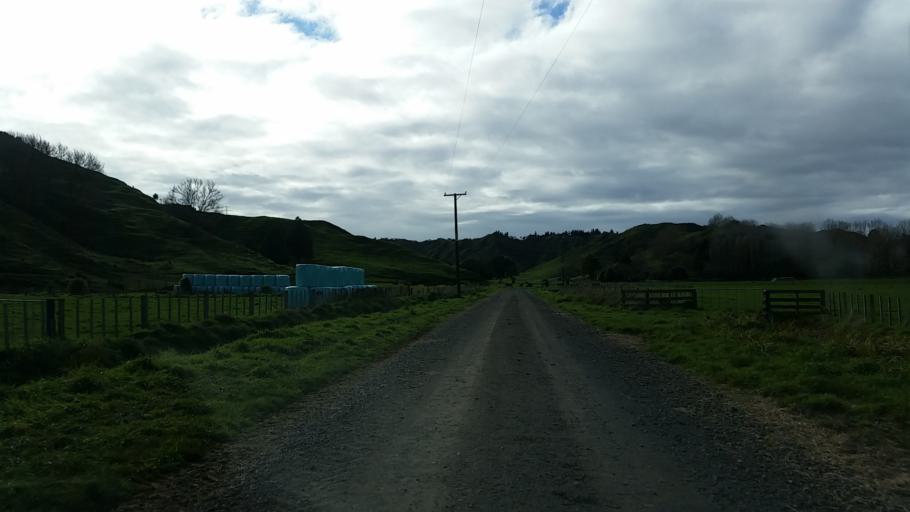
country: NZ
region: Taranaki
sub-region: South Taranaki District
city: Eltham
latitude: -39.2513
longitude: 174.5347
